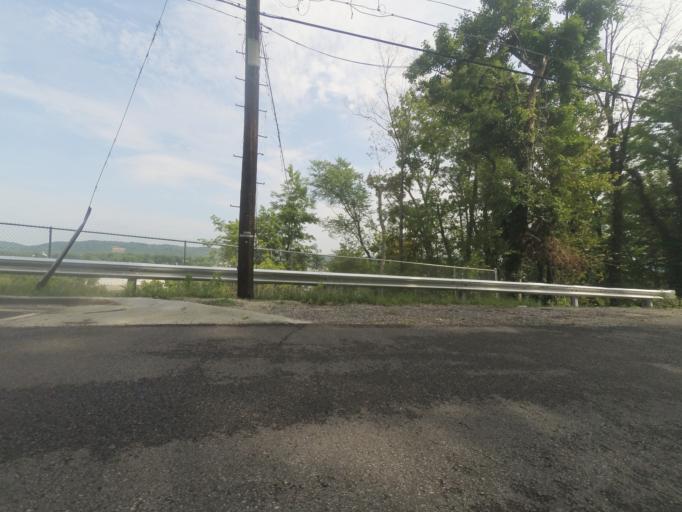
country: US
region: West Virginia
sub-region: Cabell County
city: Huntington
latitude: 38.4050
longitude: -82.4625
